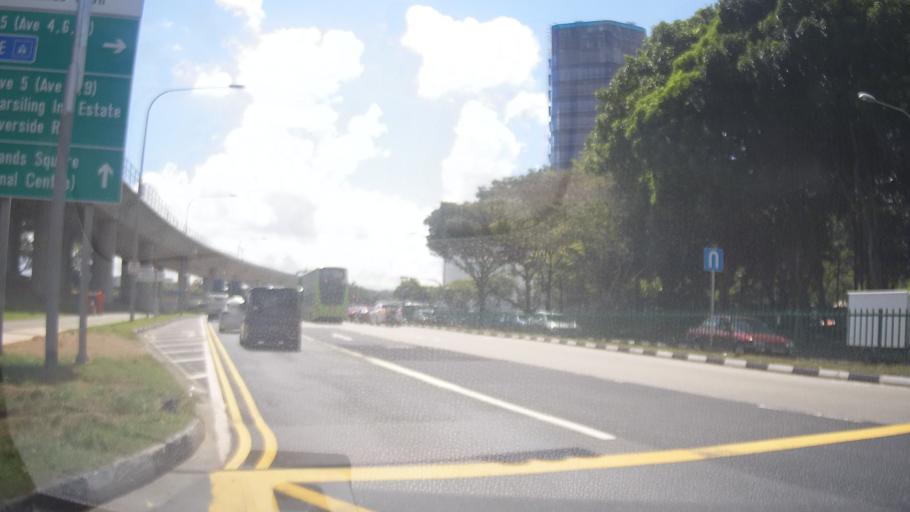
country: MY
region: Johor
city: Johor Bahru
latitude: 1.4346
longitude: 103.7823
